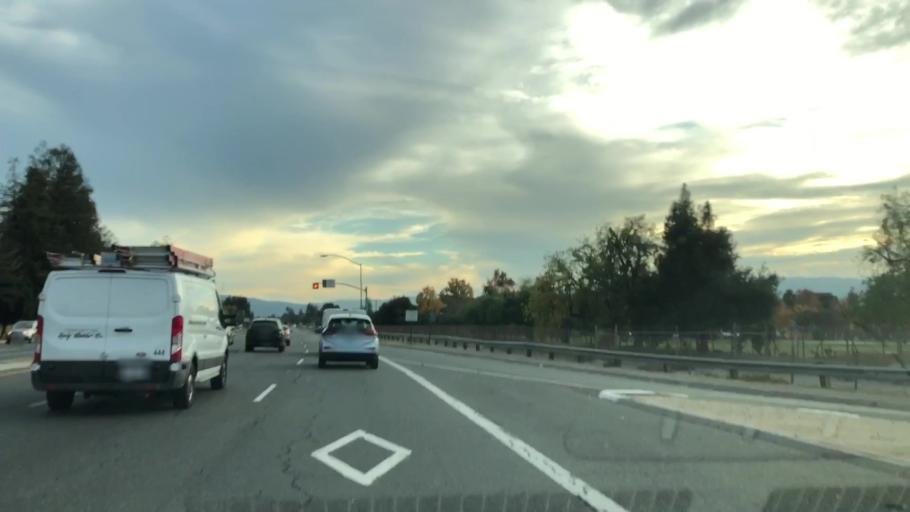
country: US
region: California
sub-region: Santa Clara County
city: Campbell
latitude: 37.3085
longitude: -121.9638
